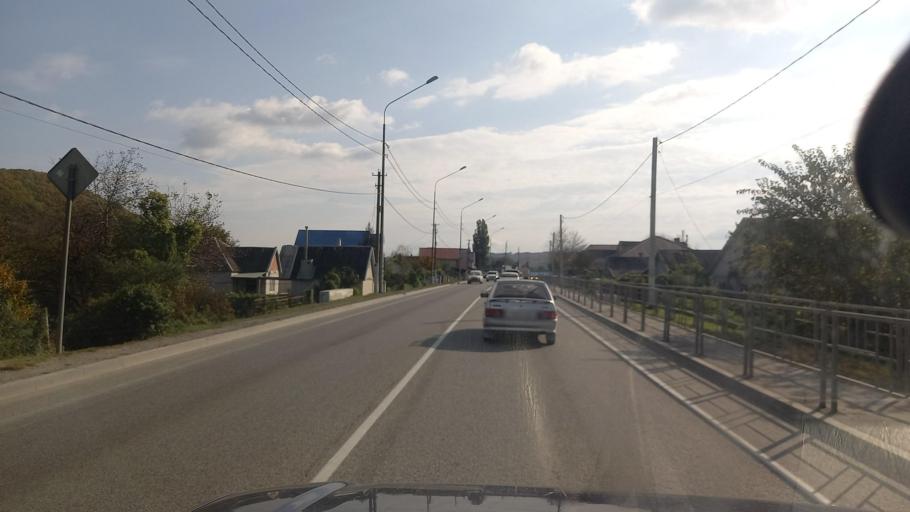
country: RU
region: Krasnodarskiy
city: Krymsk
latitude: 44.8685
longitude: 37.8504
